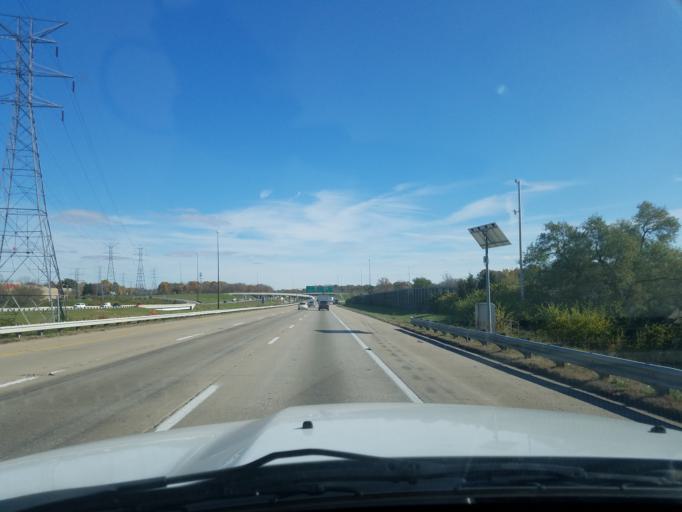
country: US
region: Indiana
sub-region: Marion County
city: Southport
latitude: 39.7004
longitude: -86.1573
